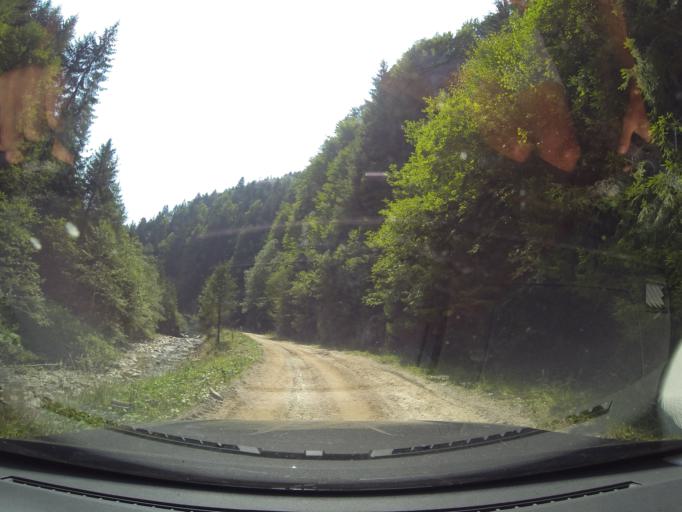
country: RO
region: Arges
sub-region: Comuna Arefu
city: Arefu
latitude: 45.4700
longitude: 24.6336
